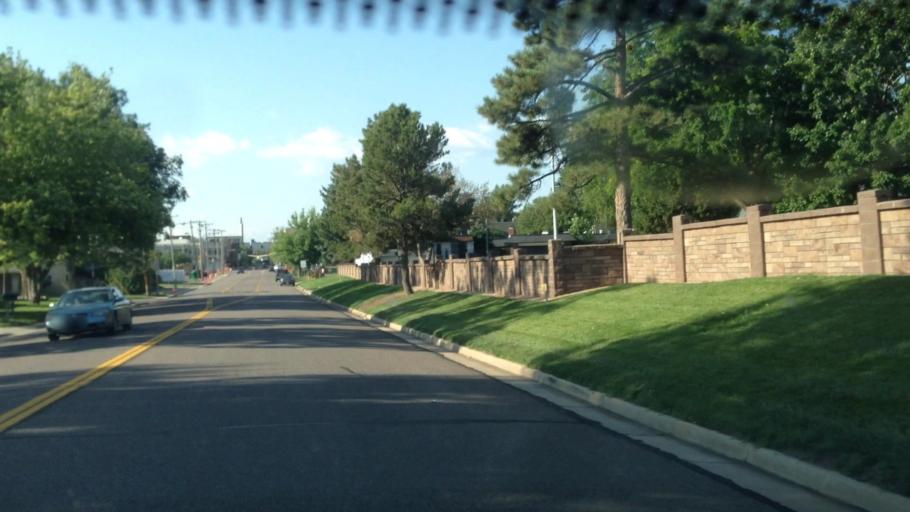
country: US
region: Colorado
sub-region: Jefferson County
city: Lakewood
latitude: 39.7138
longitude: -105.0769
